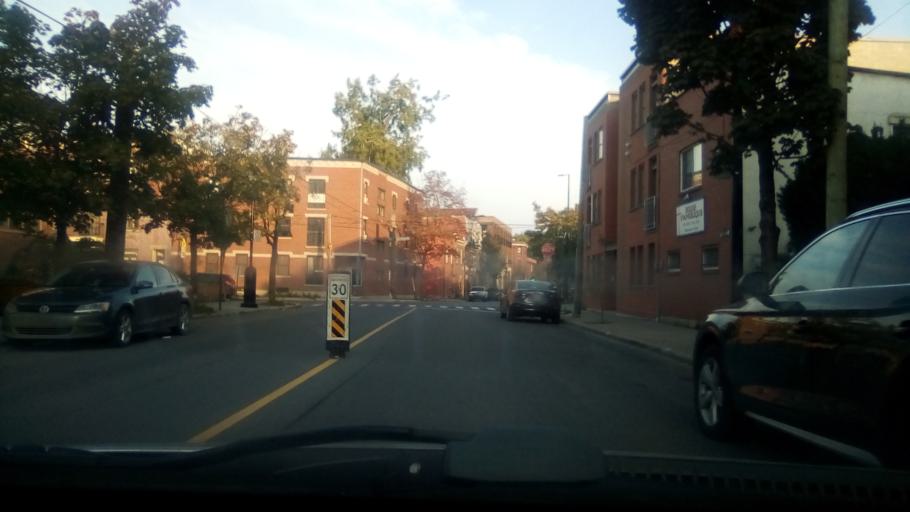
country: CA
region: Quebec
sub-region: Montreal
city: Montreal
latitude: 45.4819
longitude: -73.5608
